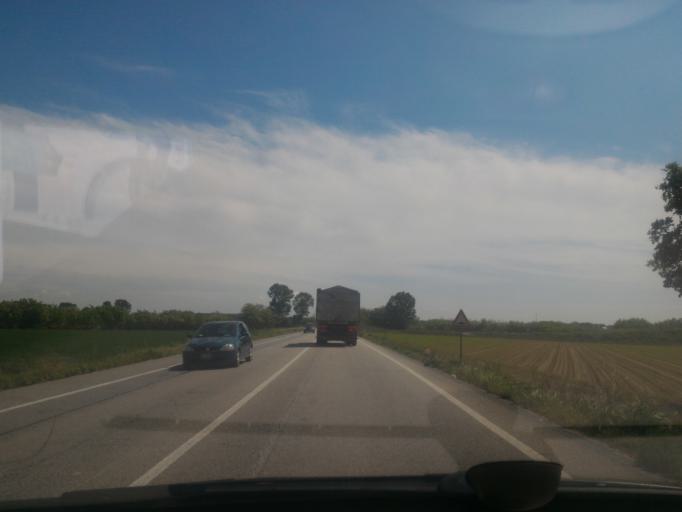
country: IT
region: Piedmont
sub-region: Provincia di Torino
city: Trofarello
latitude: 44.9593
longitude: 7.7111
